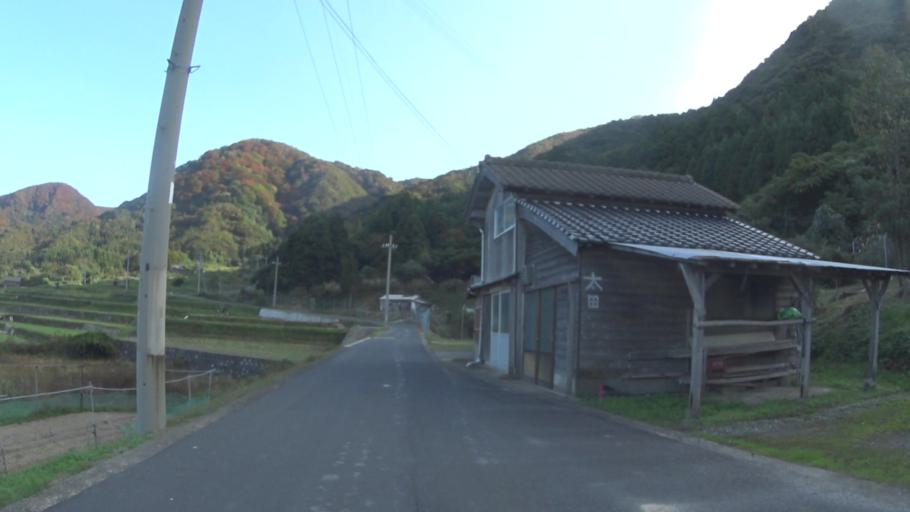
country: JP
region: Kyoto
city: Miyazu
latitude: 35.7627
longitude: 135.2002
